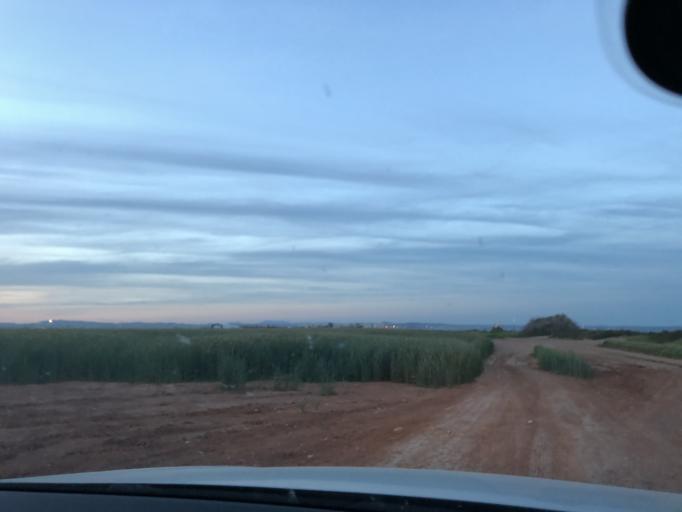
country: CY
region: Larnaka
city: Meneou
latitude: 34.8699
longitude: 33.6379
